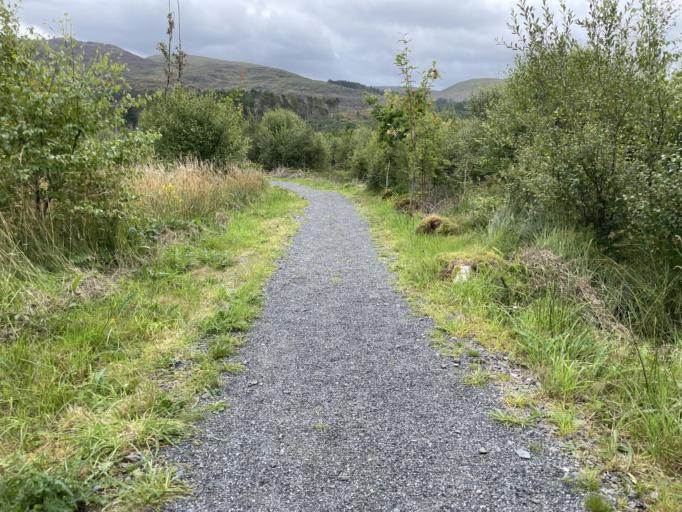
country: GB
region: Scotland
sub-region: Dumfries and Galloway
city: Newton Stewart
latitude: 55.0872
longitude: -4.5048
